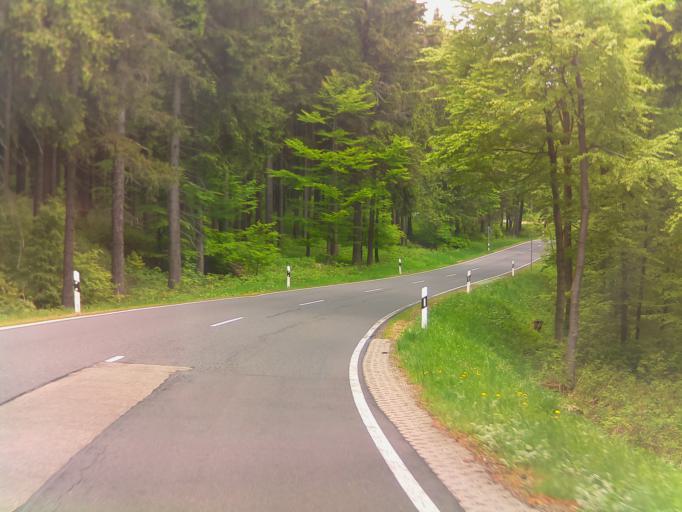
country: DE
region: Thuringia
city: Schmiedefeld am Rennsteig
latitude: 50.6187
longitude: 10.7704
